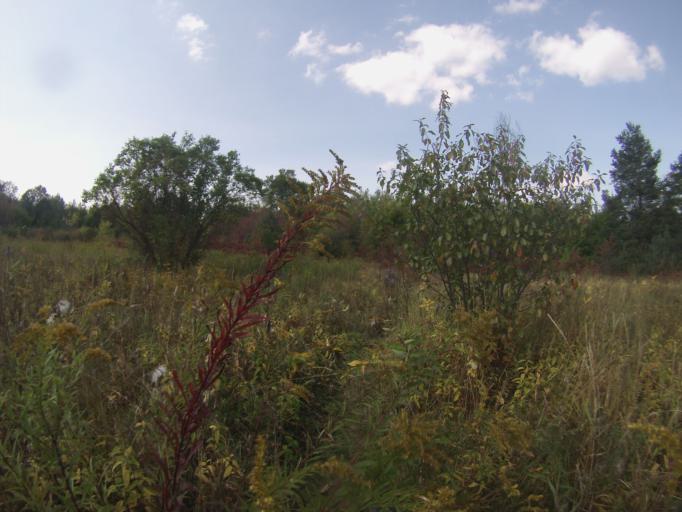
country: CA
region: Ontario
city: Ottawa
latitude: 45.3571
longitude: -75.6206
